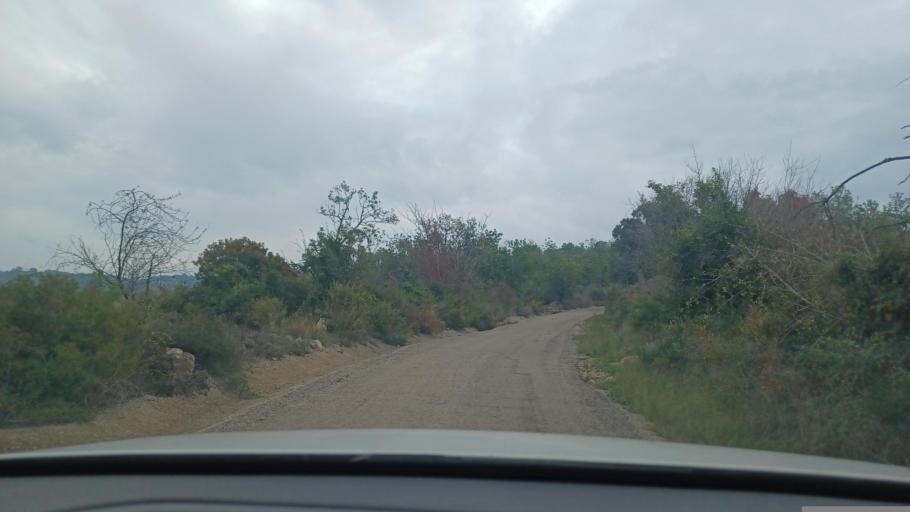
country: ES
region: Catalonia
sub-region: Provincia de Tarragona
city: Ulldecona
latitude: 40.6502
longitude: 0.4694
